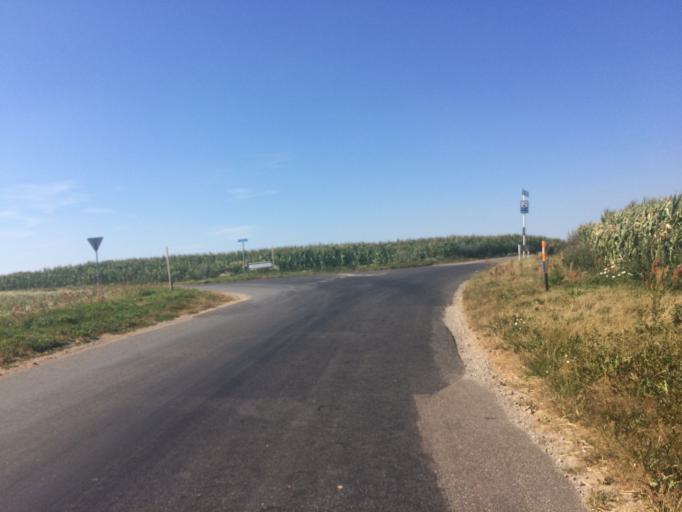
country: DK
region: Central Jutland
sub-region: Holstebro Kommune
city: Vinderup
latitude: 56.5671
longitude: 8.7571
